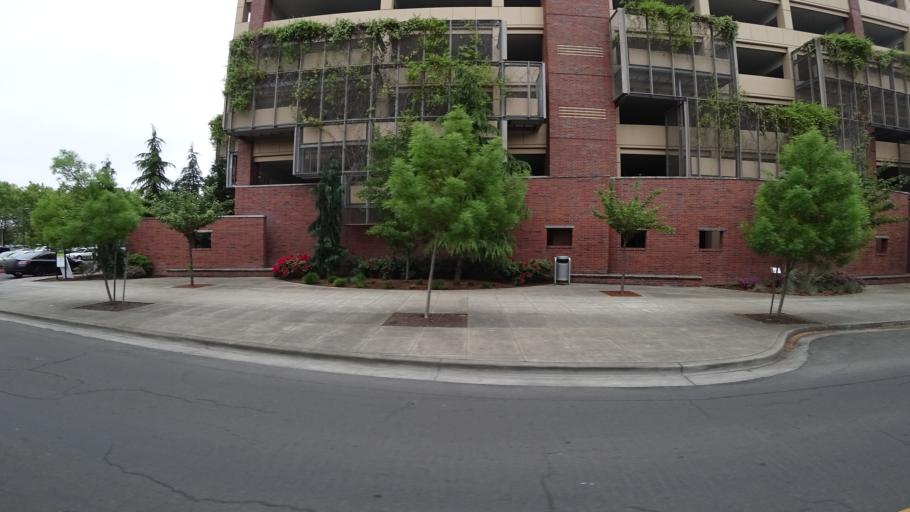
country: US
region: Oregon
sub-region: Washington County
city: Rockcreek
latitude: 45.5408
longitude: -122.8771
